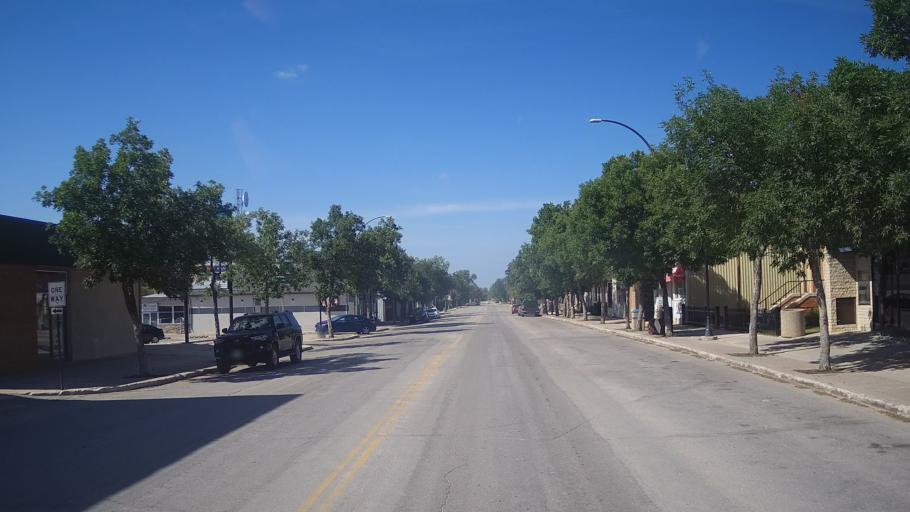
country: CA
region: Manitoba
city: Stonewall
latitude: 50.1348
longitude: -97.3266
